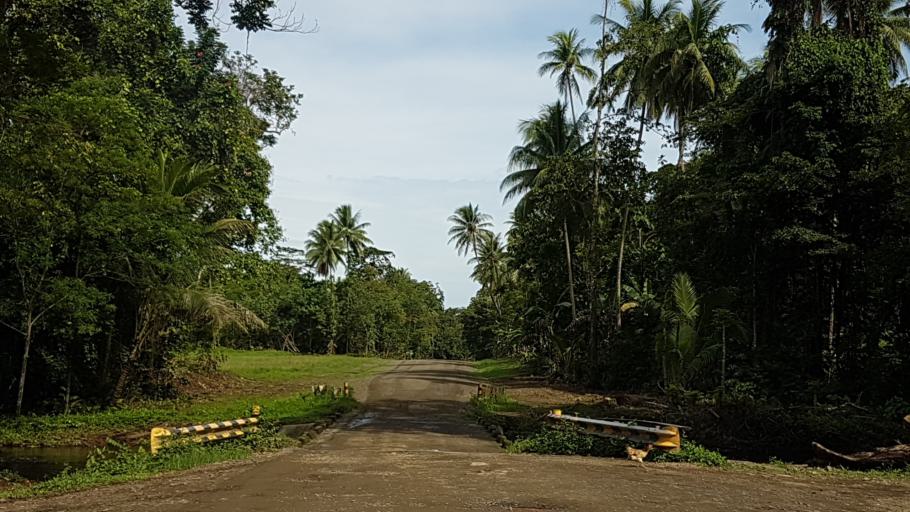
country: PG
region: Milne Bay
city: Alotau
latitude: -10.3369
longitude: 150.5459
